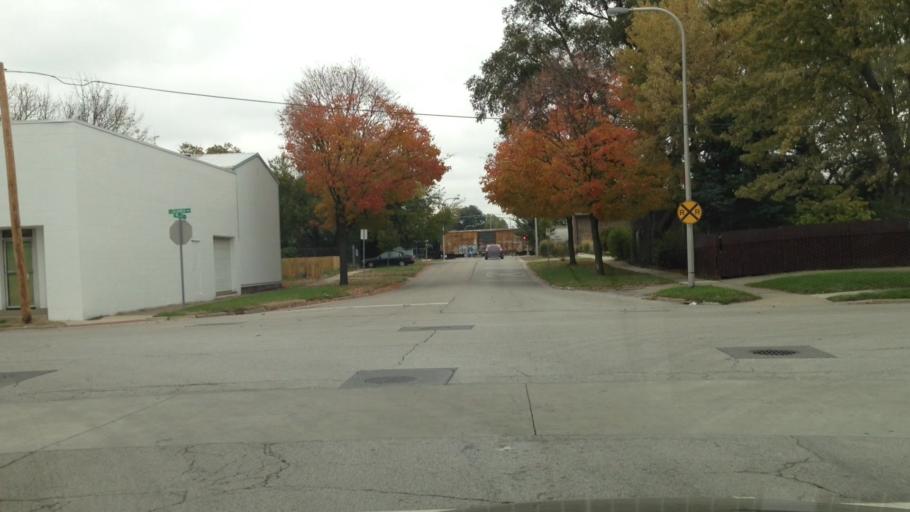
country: US
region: Illinois
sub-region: Champaign County
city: Champaign
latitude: 40.1210
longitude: -88.2412
